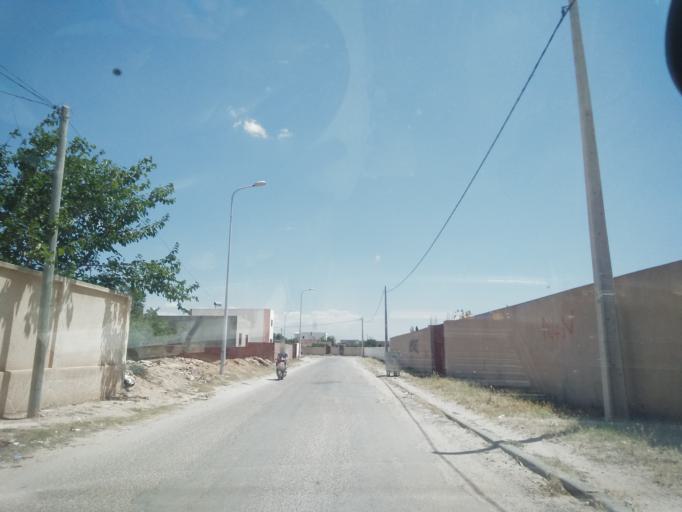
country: TN
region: Safaqis
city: Al Qarmadah
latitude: 34.8237
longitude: 10.7699
